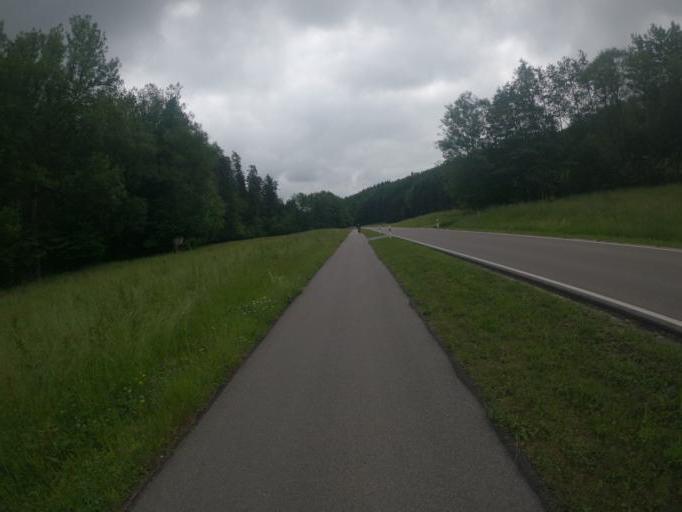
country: DE
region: Baden-Wuerttemberg
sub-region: Regierungsbezirk Stuttgart
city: Ebersbach an der Fils
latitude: 48.7356
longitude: 9.5480
